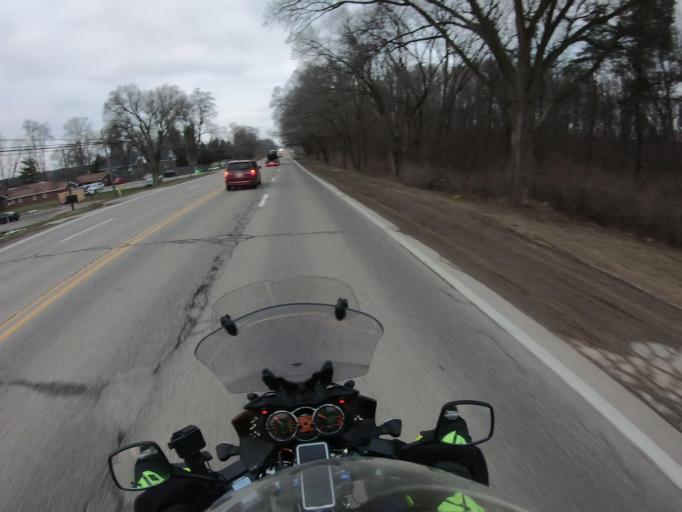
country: US
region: Michigan
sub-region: Oakland County
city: Clarkston
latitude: 42.7683
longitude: -83.4857
